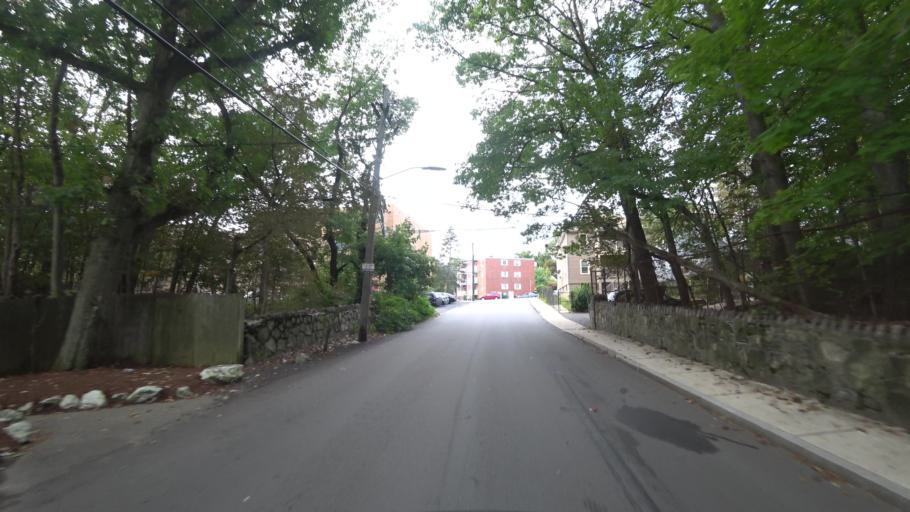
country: US
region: Massachusetts
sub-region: Suffolk County
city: Jamaica Plain
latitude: 42.2739
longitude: -71.1078
